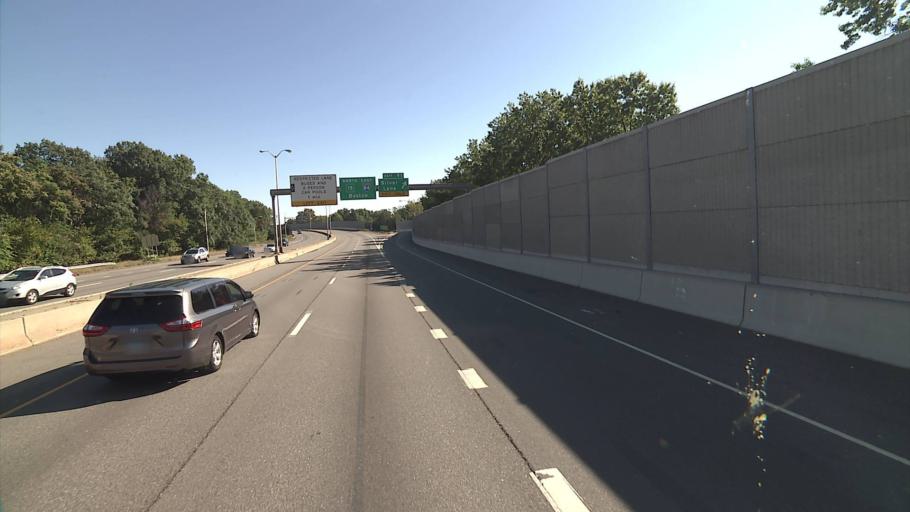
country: US
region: Connecticut
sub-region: Hartford County
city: East Hartford
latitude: 41.7594
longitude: -72.6410
